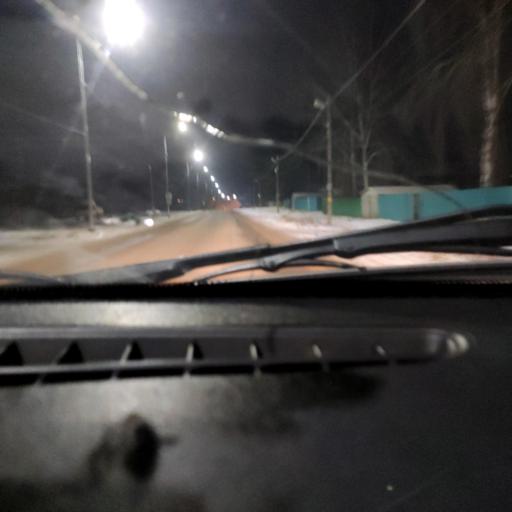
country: RU
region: Bashkortostan
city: Avdon
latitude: 54.6102
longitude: 55.8424
